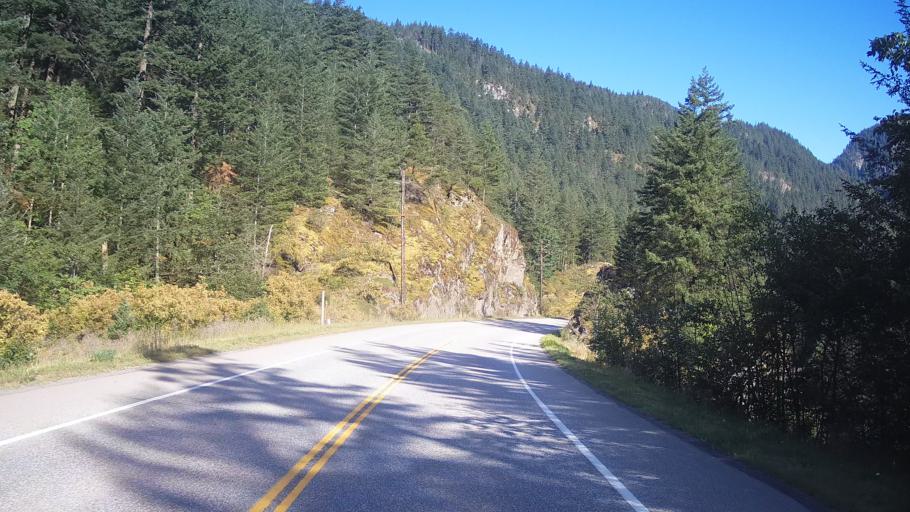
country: CA
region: British Columbia
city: Hope
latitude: 49.5963
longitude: -121.4127
